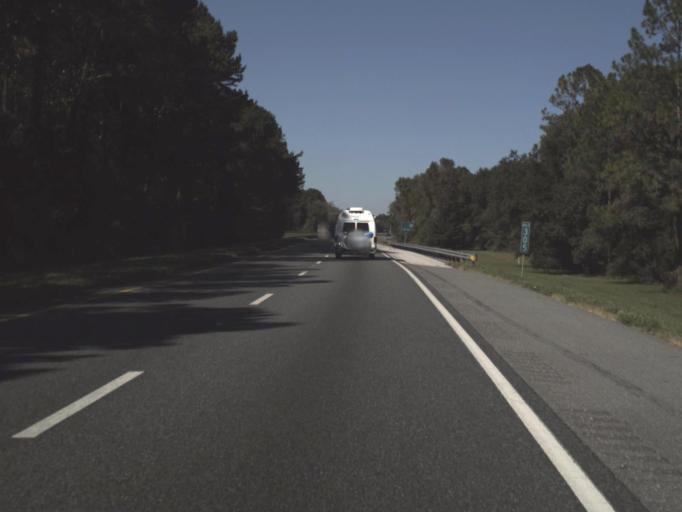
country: US
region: Florida
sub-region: Sumter County
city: Wildwood
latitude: 28.8331
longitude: -82.0372
